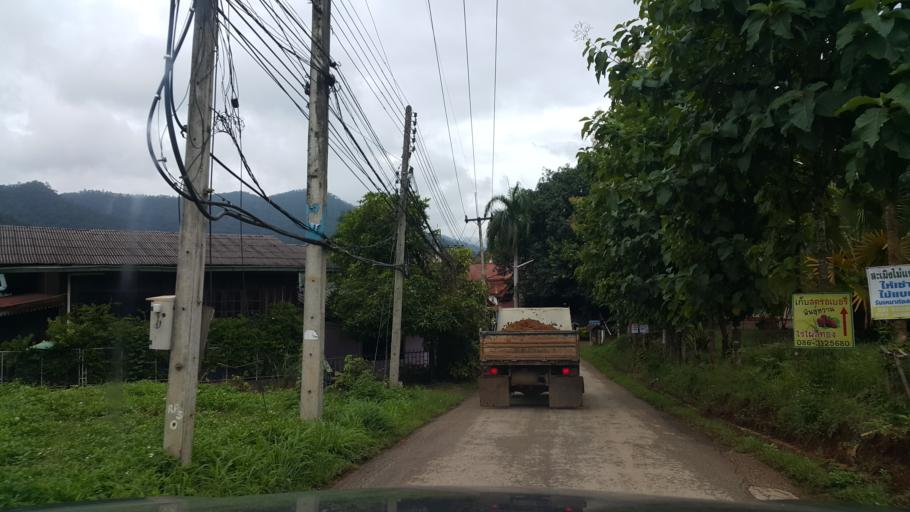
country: TH
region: Chiang Mai
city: Samoeng
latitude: 18.8570
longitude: 98.7319
